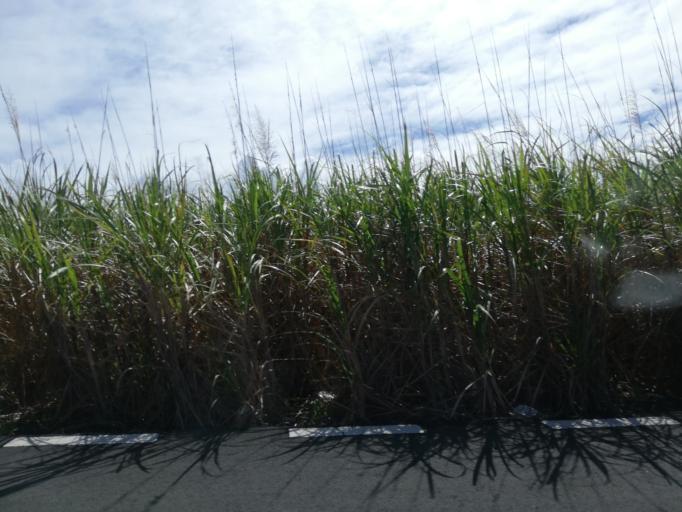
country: MU
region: Grand Port
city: Plaine Magnien
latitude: -20.4532
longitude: 57.6749
